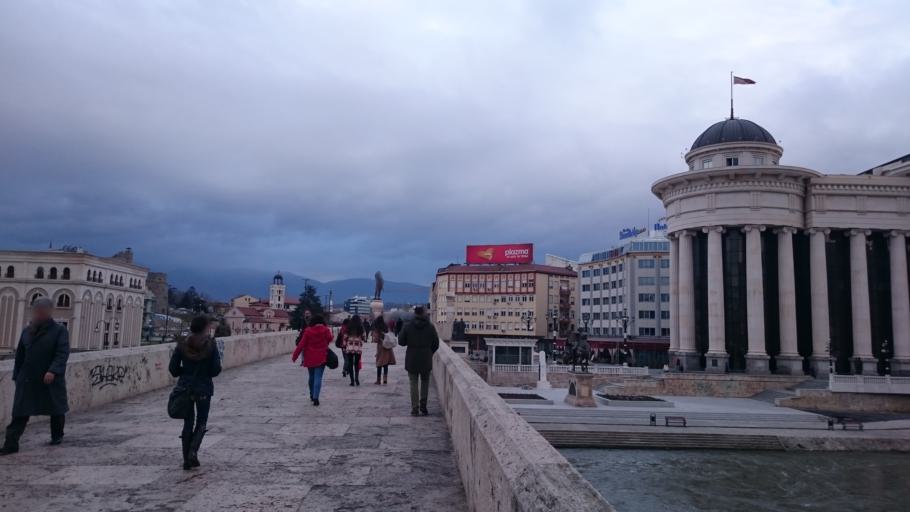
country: MK
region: Karpos
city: Skopje
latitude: 41.9968
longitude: 21.4328
